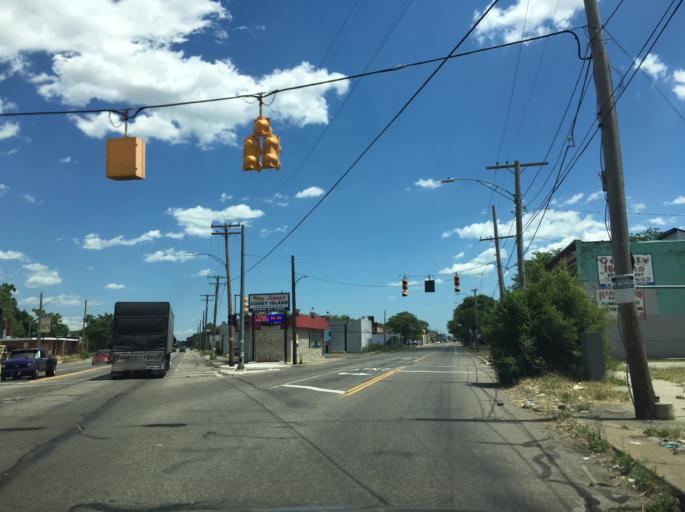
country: US
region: Michigan
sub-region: Wayne County
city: Hamtramck
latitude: 42.4188
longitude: -83.0527
